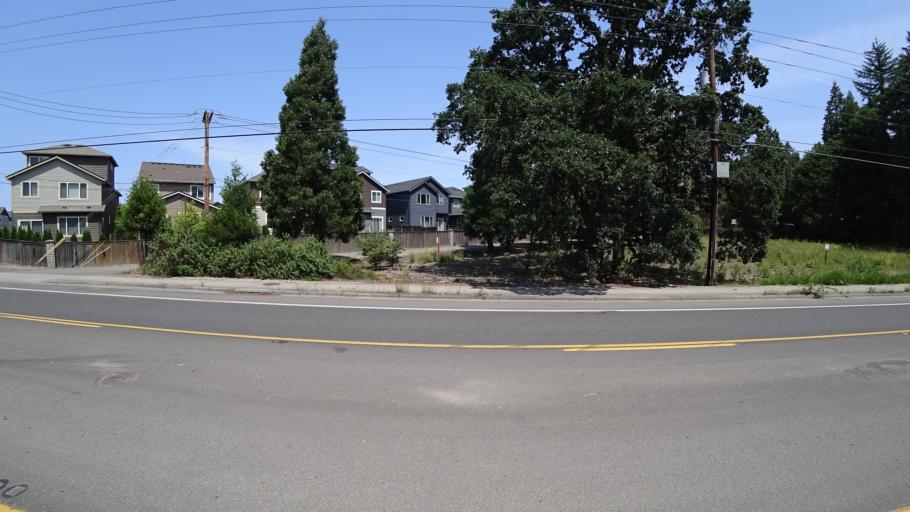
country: US
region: Oregon
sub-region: Washington County
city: Hillsboro
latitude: 45.4958
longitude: -122.9415
